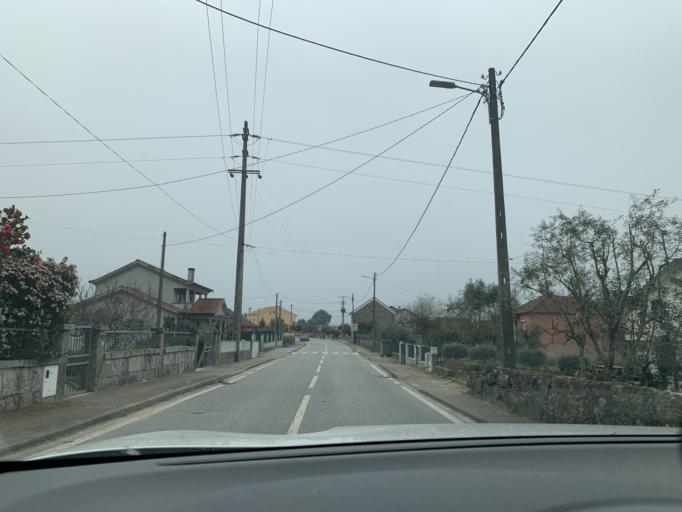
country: PT
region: Viseu
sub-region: Concelho de Tondela
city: Tondela
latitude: 40.4999
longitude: -8.0755
